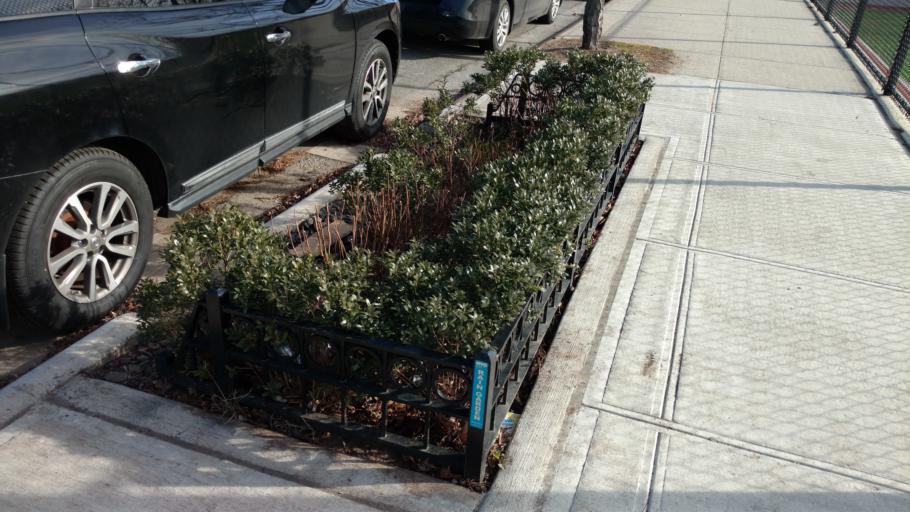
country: US
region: New York
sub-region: Queens County
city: Long Island City
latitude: 40.7280
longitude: -73.9046
